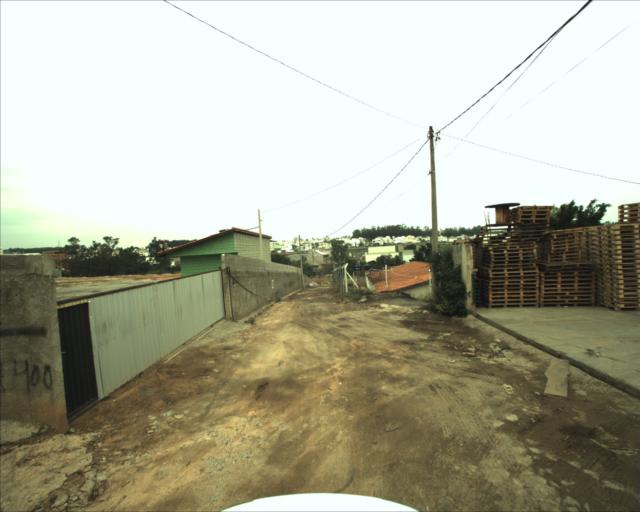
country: BR
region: Sao Paulo
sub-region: Sorocaba
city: Sorocaba
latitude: -23.4675
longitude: -47.4180
